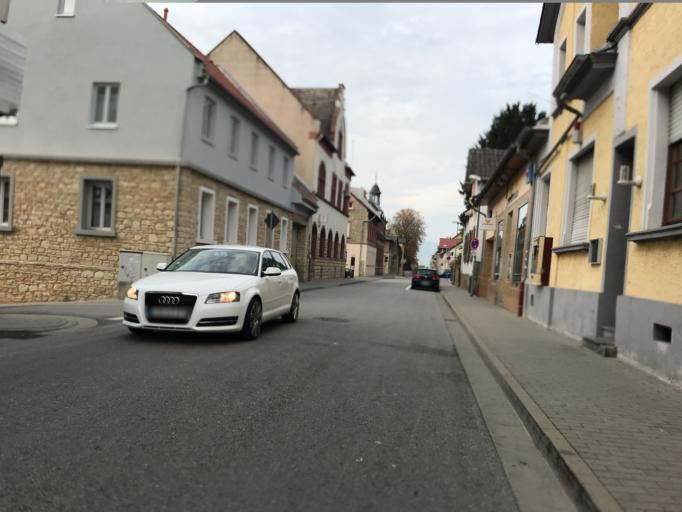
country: DE
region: Rheinland-Pfalz
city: Ingelheim am Rhein
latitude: 49.9660
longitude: 8.0592
